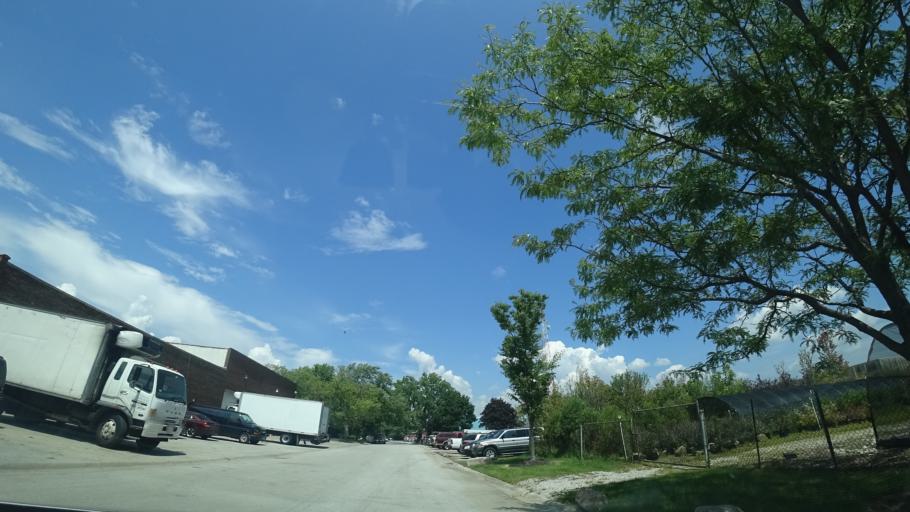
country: US
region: Illinois
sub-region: Cook County
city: Robbins
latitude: 41.6628
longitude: -87.7163
